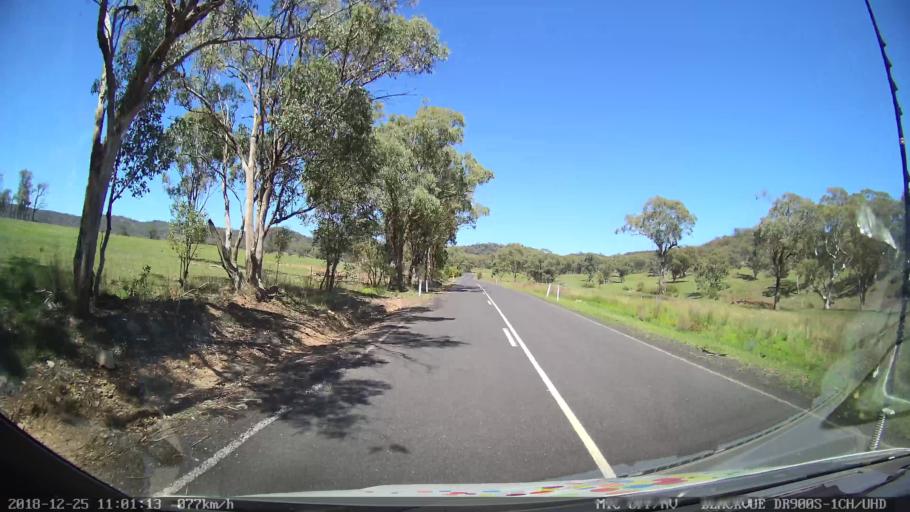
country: AU
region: New South Wales
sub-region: Upper Hunter Shire
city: Merriwa
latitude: -32.4039
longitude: 150.2046
